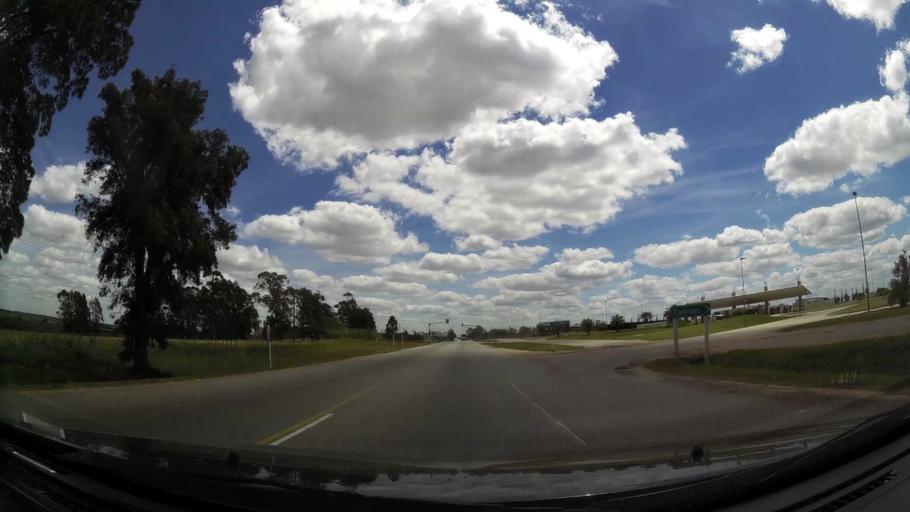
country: UY
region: Canelones
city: Colonia Nicolich
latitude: -34.8137
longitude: -56.0071
